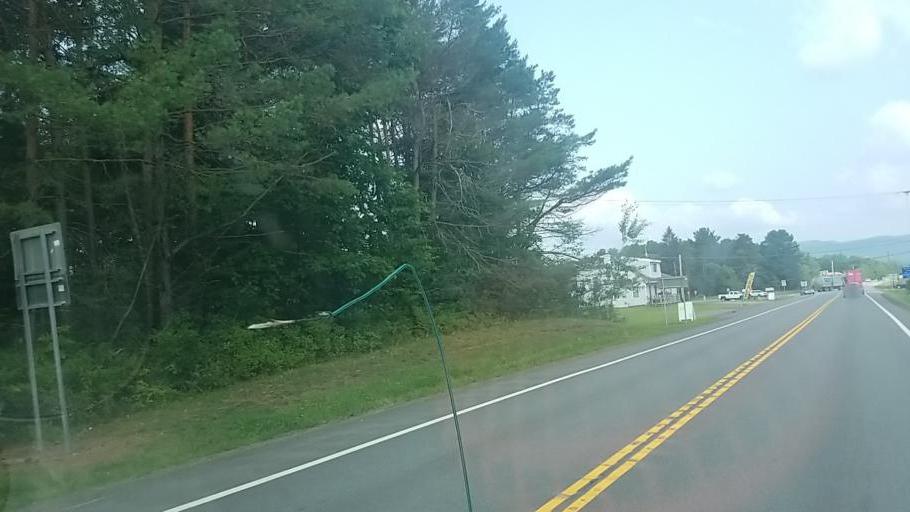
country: US
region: New York
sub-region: Fulton County
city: Broadalbin
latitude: 43.0755
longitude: -74.2579
